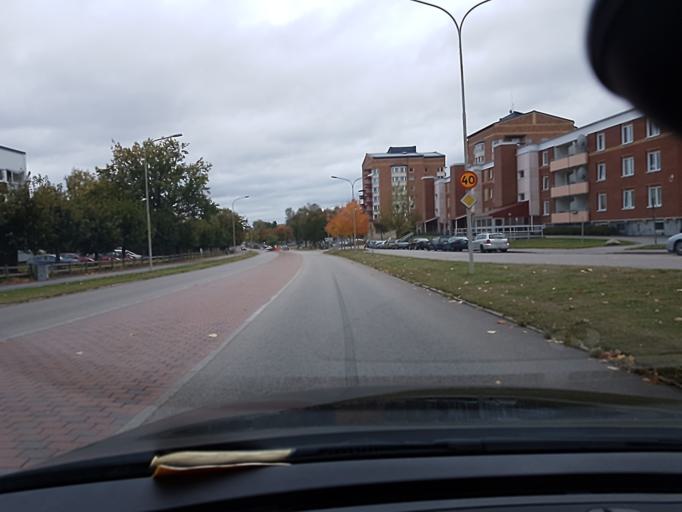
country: SE
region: Kronoberg
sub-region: Vaxjo Kommun
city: Vaexjoe
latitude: 56.8923
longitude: 14.7988
